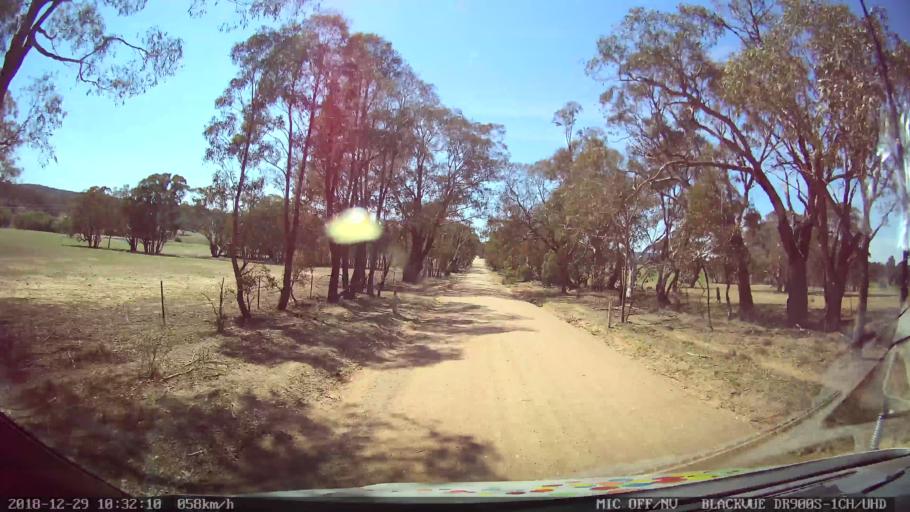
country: AU
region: New South Wales
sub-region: Yass Valley
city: Gundaroo
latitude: -34.9731
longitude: 149.4622
